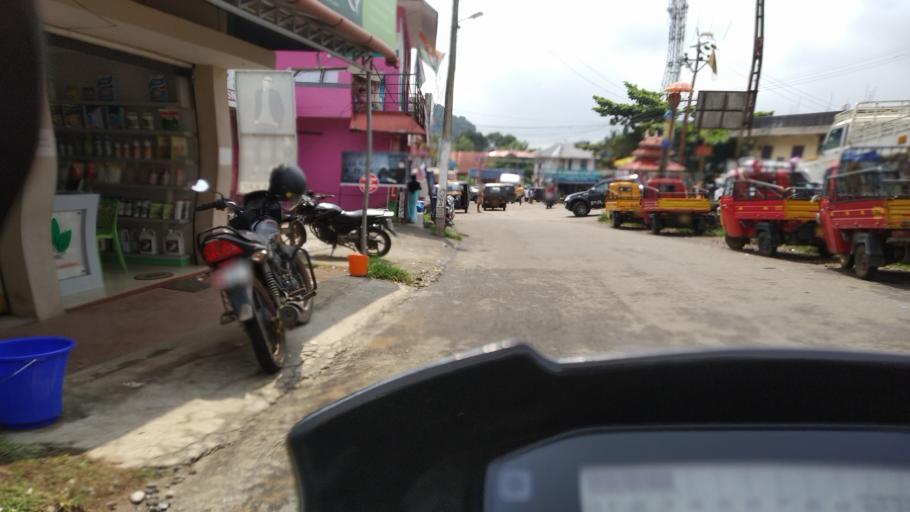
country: IN
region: Kerala
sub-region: Kottayam
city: Erattupetta
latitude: 9.6301
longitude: 76.9789
